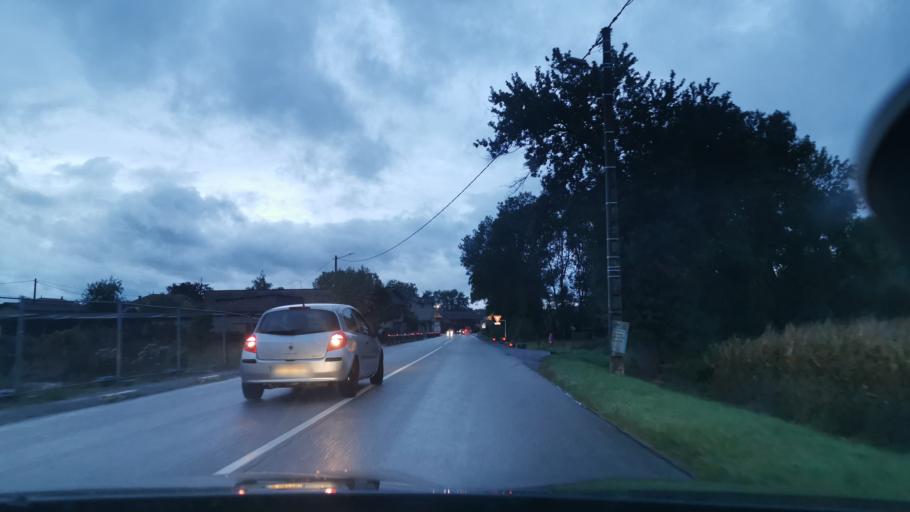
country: FR
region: Rhone-Alpes
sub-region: Departement de l'Ain
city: Pont-de-Veyle
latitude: 46.2560
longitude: 4.8896
